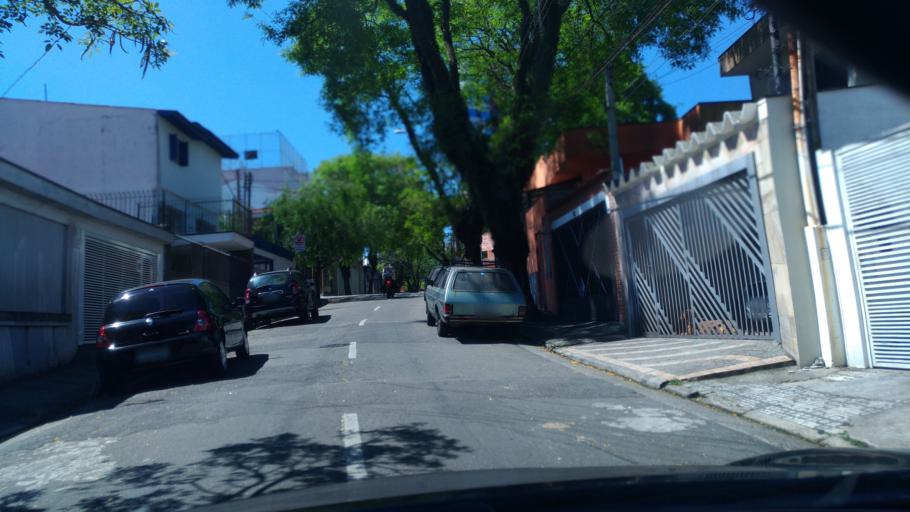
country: BR
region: Sao Paulo
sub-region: Sao Bernardo Do Campo
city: Sao Bernardo do Campo
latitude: -23.6944
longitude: -46.5558
